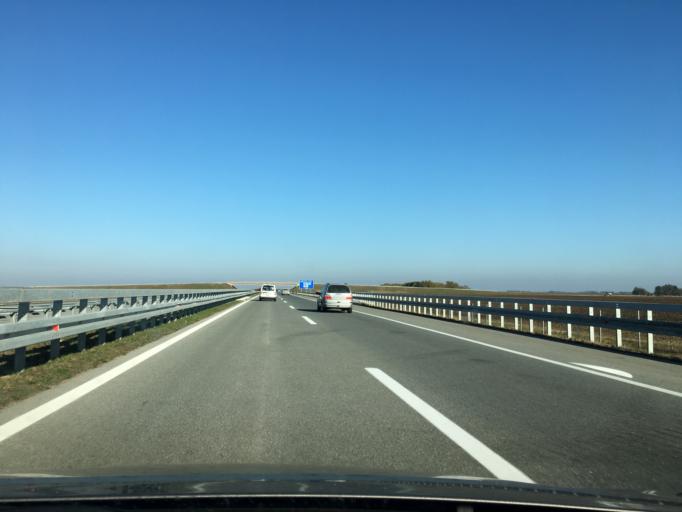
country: RS
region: Autonomna Pokrajina Vojvodina
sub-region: Severnobacki Okrug
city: Mali Igos
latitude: 45.7444
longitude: 19.7027
